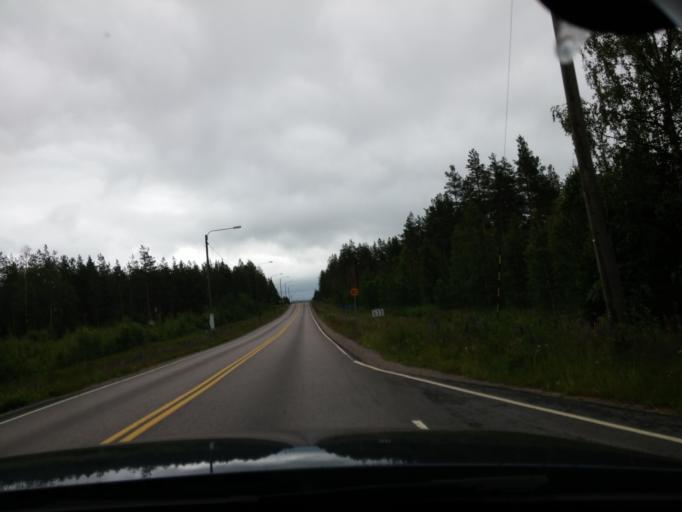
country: FI
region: Central Finland
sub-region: Saarijaervi-Viitasaari
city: Pylkoenmaeki
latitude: 62.6367
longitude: 24.8215
